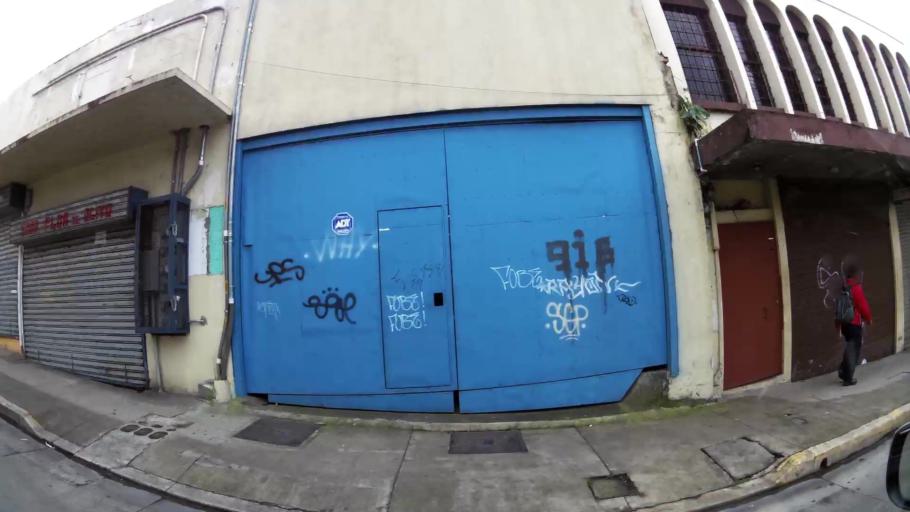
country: CR
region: San Jose
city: San Jose
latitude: 9.9307
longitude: -84.0806
